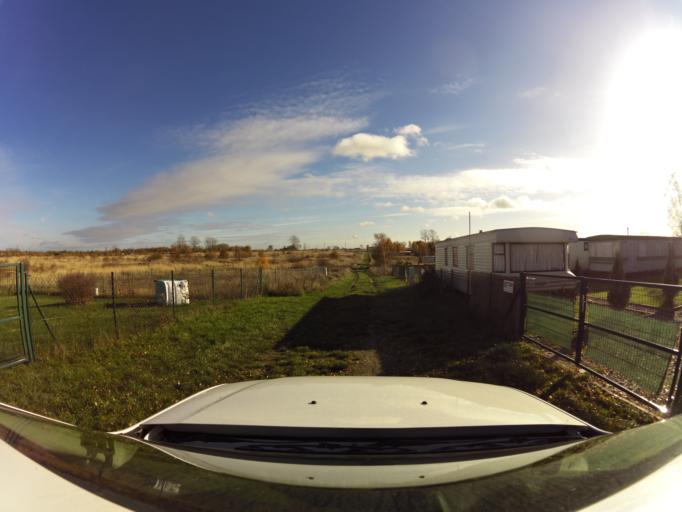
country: PL
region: West Pomeranian Voivodeship
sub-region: Powiat gryficki
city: Rewal
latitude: 54.0845
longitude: 15.0426
